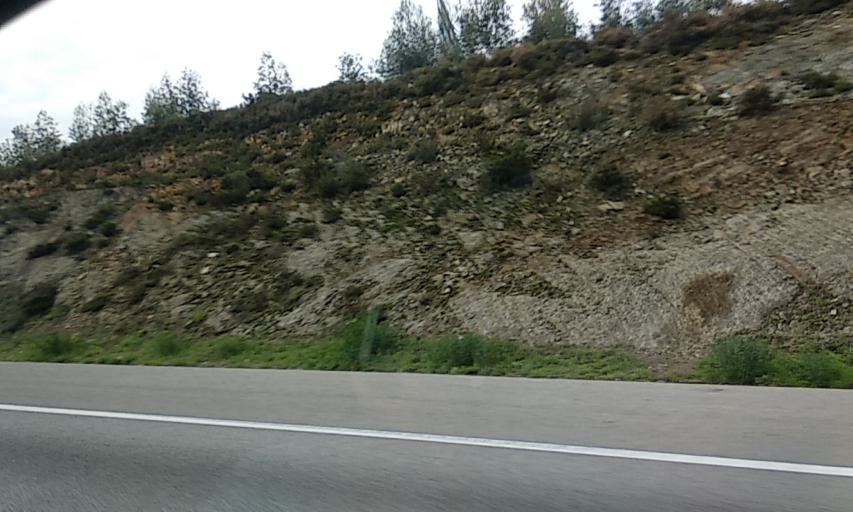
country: PT
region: Porto
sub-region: Trofa
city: Bougado
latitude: 41.3280
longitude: -8.5174
